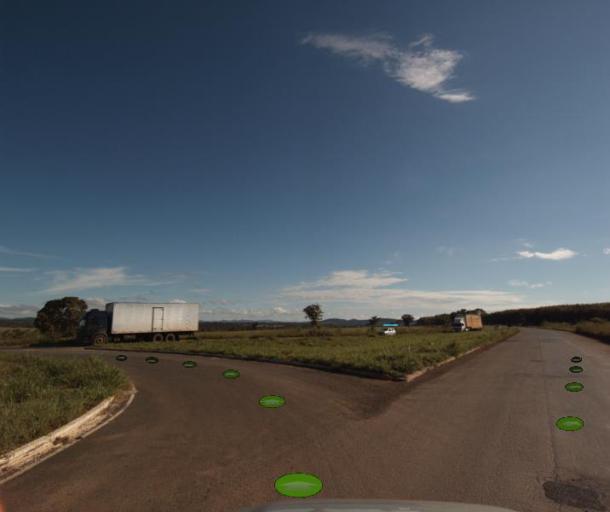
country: BR
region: Goias
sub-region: Uruacu
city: Uruacu
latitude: -14.6345
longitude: -49.1760
